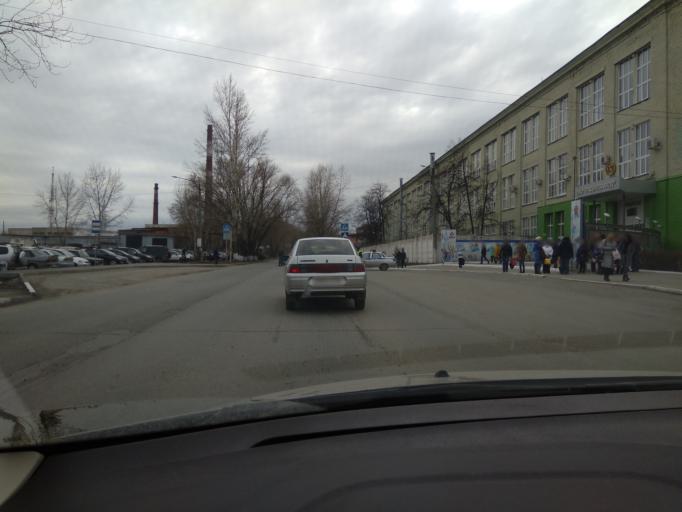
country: RU
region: Chelyabinsk
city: Kyshtym
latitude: 55.7080
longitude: 60.5743
